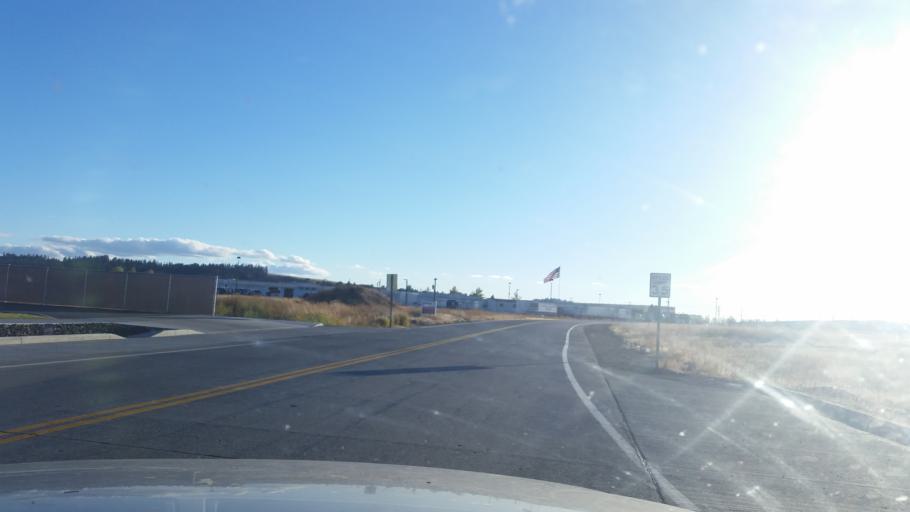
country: US
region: Washington
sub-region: Spokane County
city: Airway Heights
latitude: 47.5888
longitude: -117.5606
